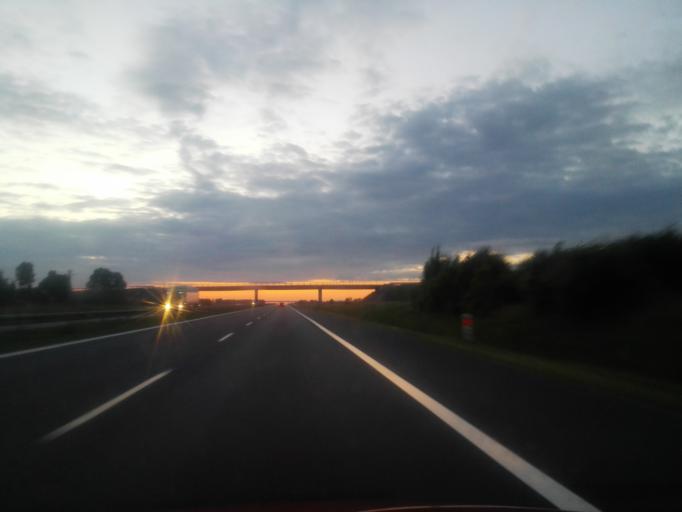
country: PL
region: Lodz Voivodeship
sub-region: Powiat piotrkowski
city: Moszczenica
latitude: 51.4758
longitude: 19.6275
